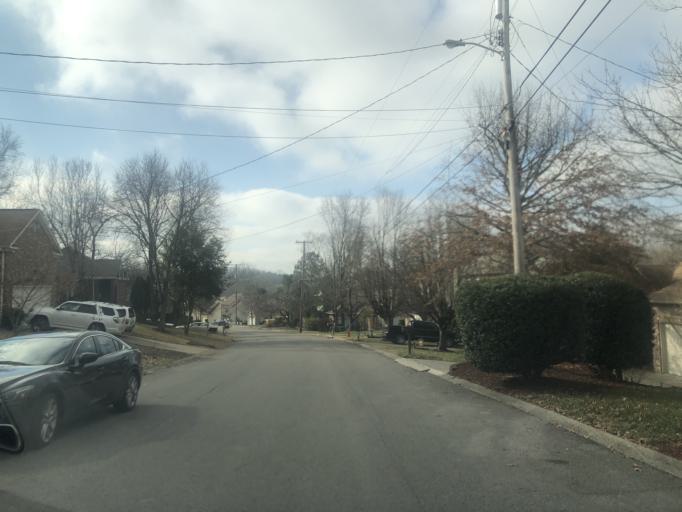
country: US
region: Tennessee
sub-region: Rutherford County
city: La Vergne
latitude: 36.0789
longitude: -86.6538
